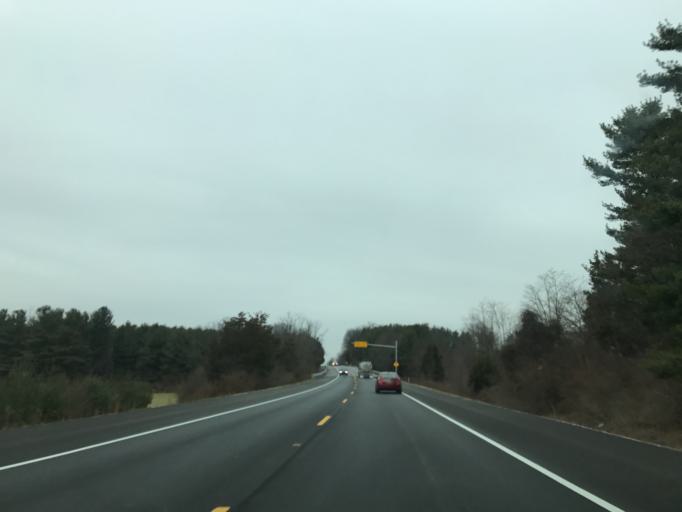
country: US
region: Maryland
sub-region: Carroll County
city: Taneytown
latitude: 39.6270
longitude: -77.1020
